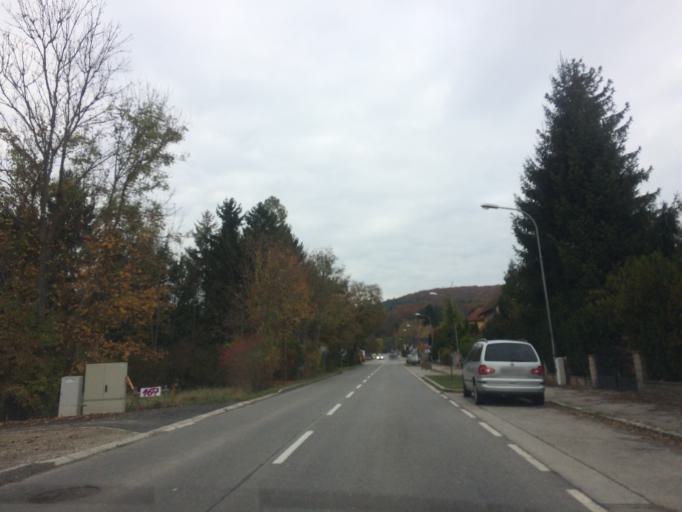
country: AT
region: Lower Austria
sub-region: Politischer Bezirk Wien-Umgebung
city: Gablitz
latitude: 48.2377
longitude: 16.1388
